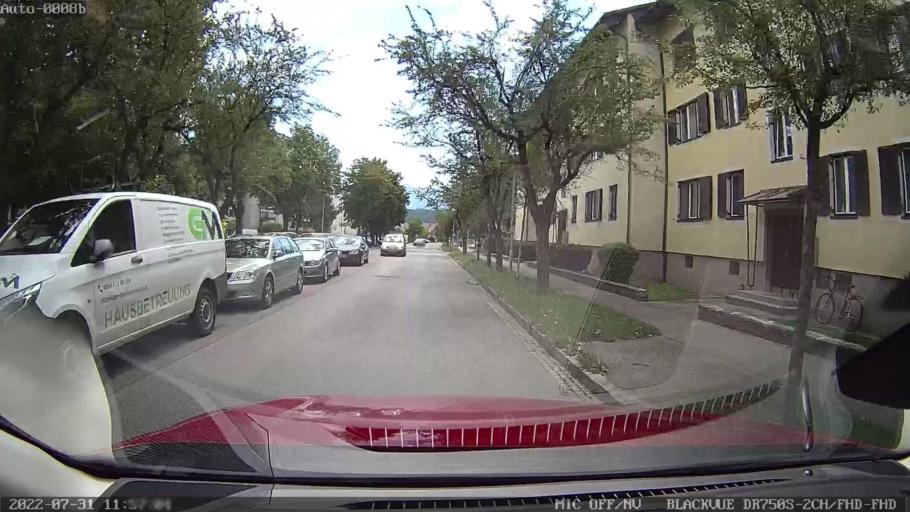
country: AT
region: Carinthia
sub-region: Villach Stadt
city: Villach
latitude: 46.6057
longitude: 13.8495
